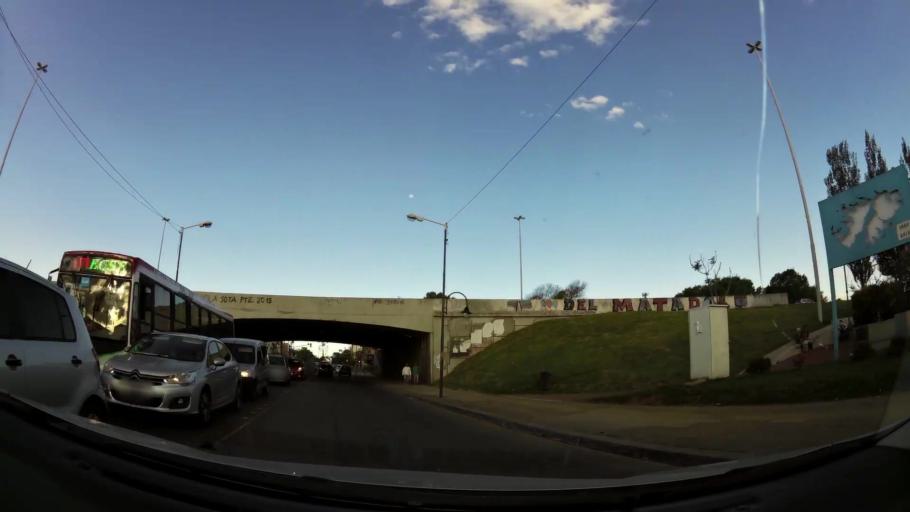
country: AR
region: Buenos Aires
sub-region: Partido de Tigre
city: Tigre
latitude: -34.4608
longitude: -58.5726
